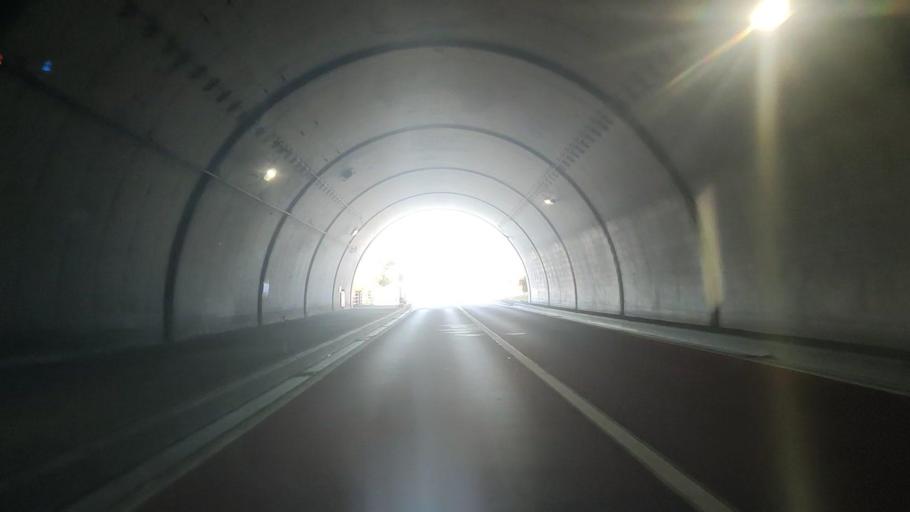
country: JP
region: Oita
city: Oita
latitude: 33.0949
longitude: 131.6506
